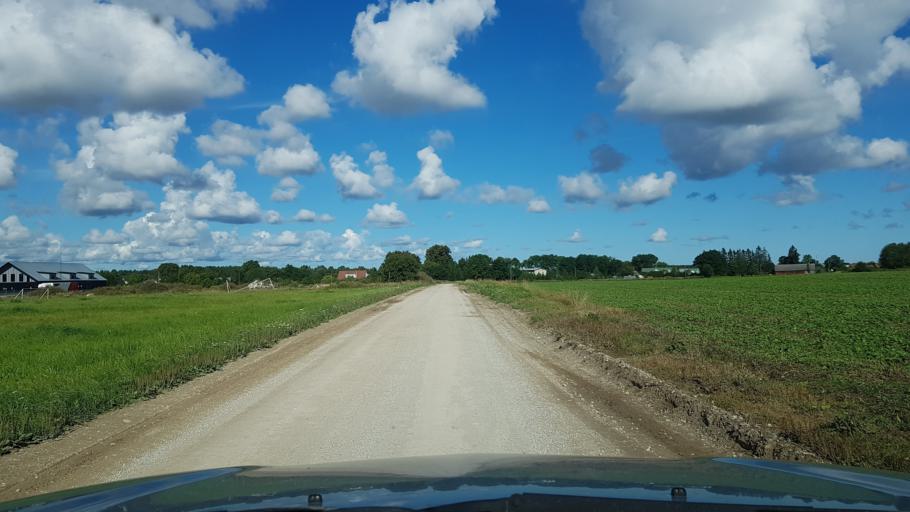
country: EE
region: Harju
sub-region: Kiili vald
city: Kiili
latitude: 59.3766
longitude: 24.8043
